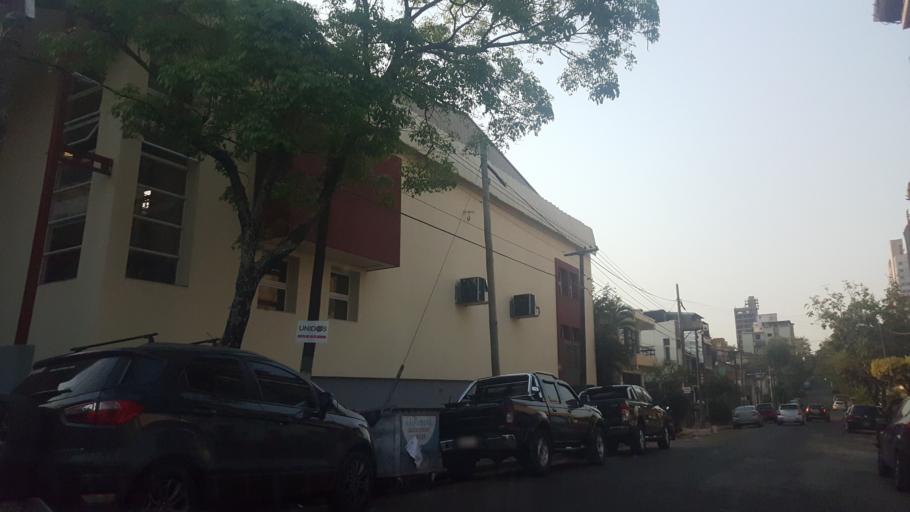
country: AR
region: Misiones
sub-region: Departamento de Capital
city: Posadas
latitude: -27.3748
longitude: -55.8914
